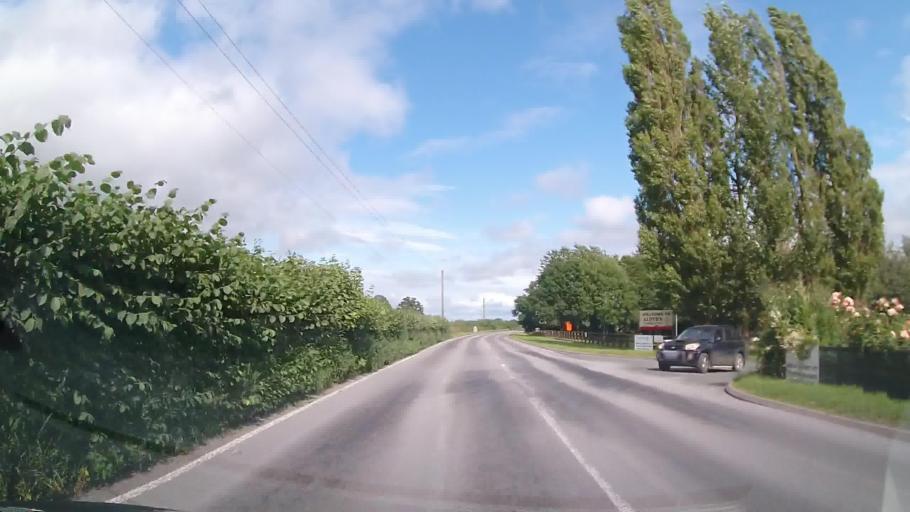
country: GB
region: England
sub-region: Shropshire
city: Pant
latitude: 52.8103
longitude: -3.0462
